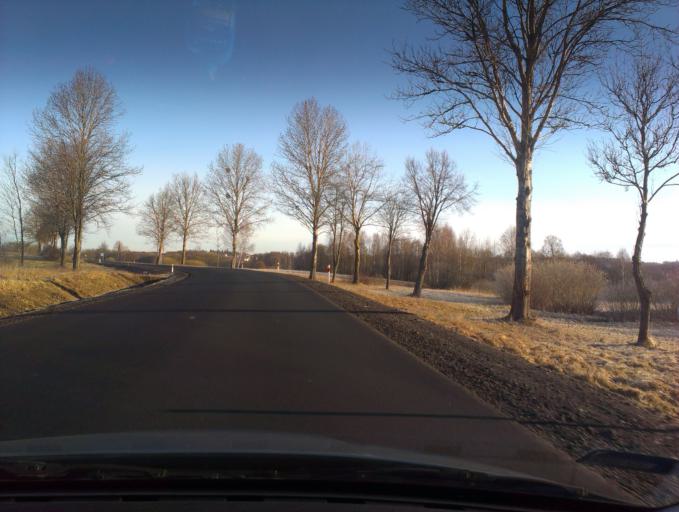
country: PL
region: West Pomeranian Voivodeship
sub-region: Powiat koszalinski
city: Bobolice
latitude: 53.9421
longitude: 16.5906
